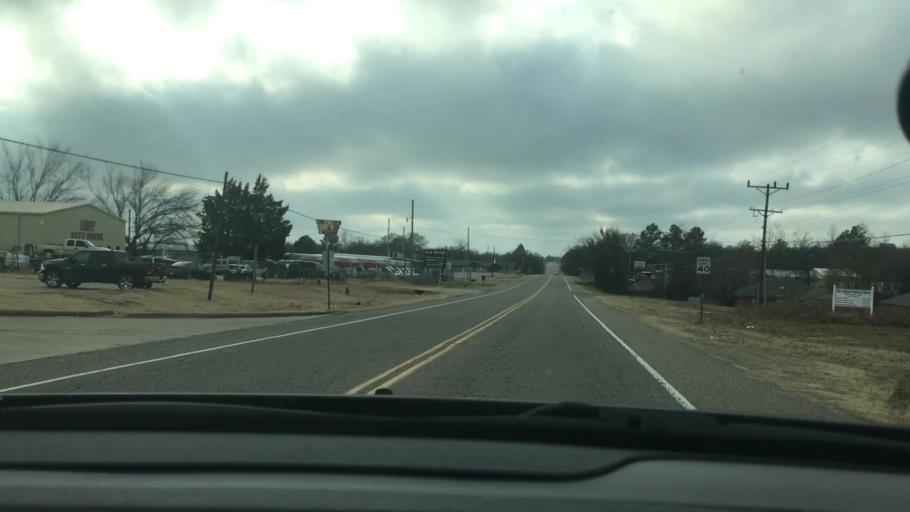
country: US
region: Oklahoma
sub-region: Bryan County
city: Durant
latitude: 34.0155
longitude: -96.3730
